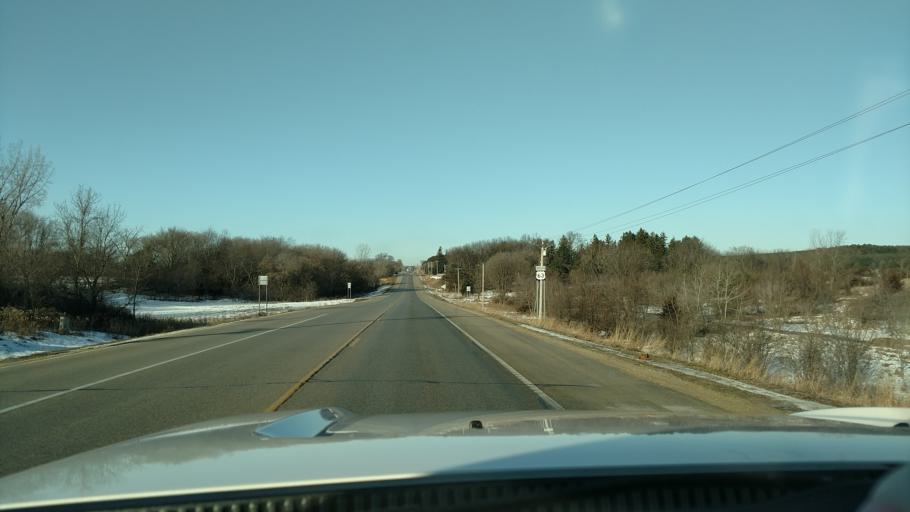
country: US
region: Minnesota
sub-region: Olmsted County
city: Oronoco
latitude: 44.1081
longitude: -92.4887
